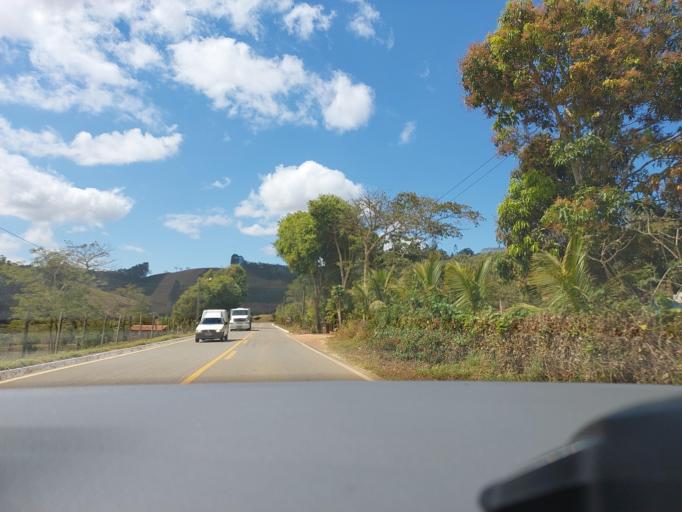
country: BR
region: Minas Gerais
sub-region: Mirai
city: Mirai
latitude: -20.9975
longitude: -42.5526
